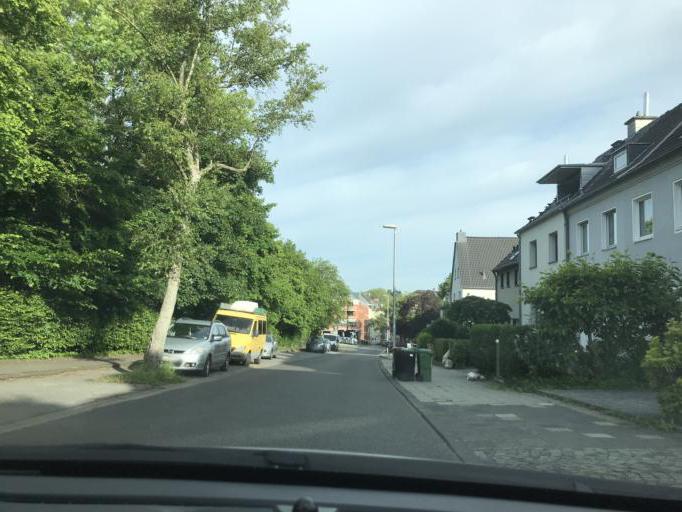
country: DE
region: North Rhine-Westphalia
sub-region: Regierungsbezirk Koln
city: Aachen
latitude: 50.7582
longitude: 6.0963
